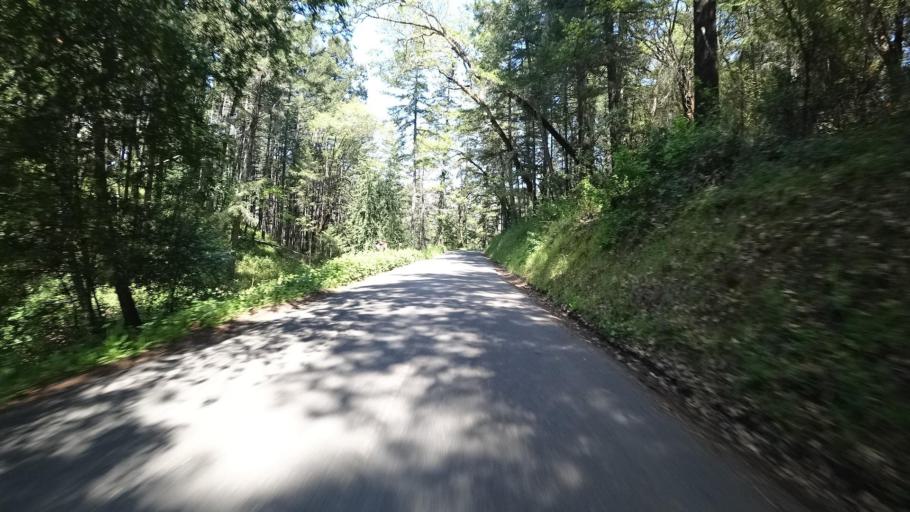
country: US
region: California
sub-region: Humboldt County
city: Redway
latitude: 40.1702
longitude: -123.6100
